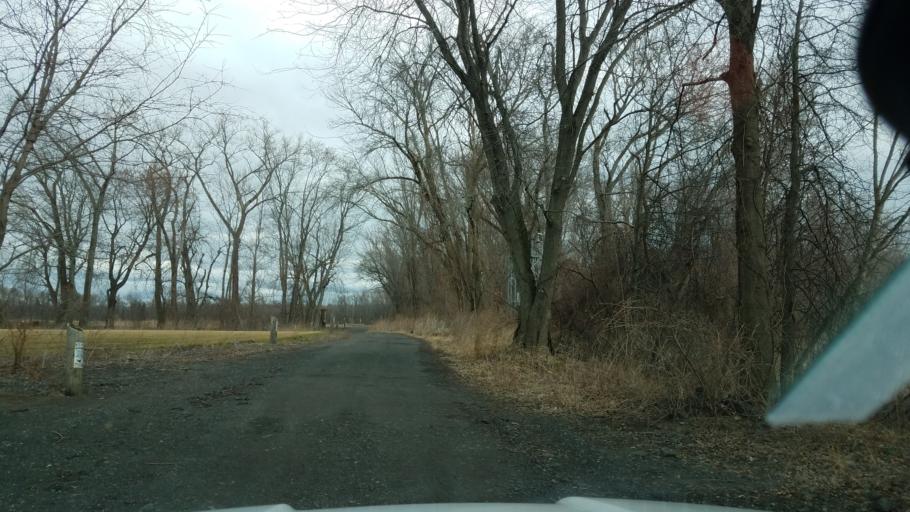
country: US
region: Connecticut
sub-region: Hartford County
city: Wethersfield
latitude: 41.6993
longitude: -72.6370
